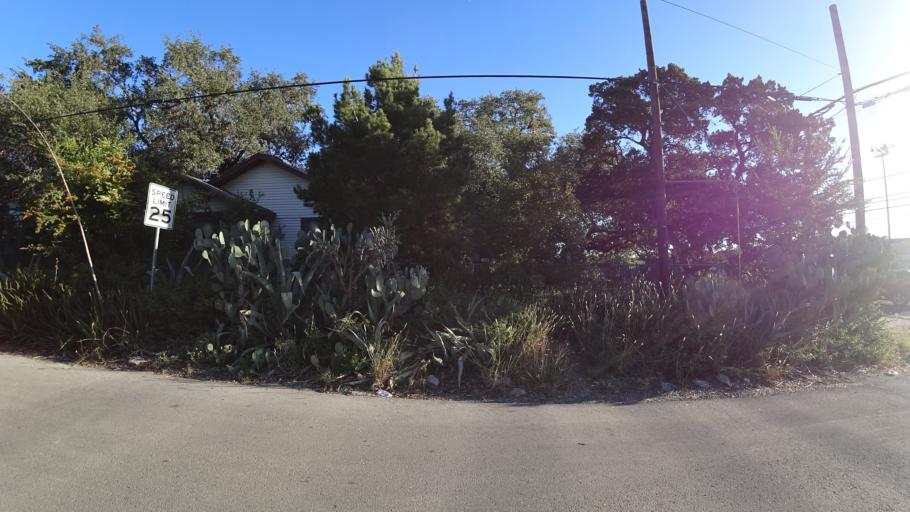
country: US
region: Texas
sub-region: Travis County
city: Austin
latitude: 30.2535
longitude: -97.7534
